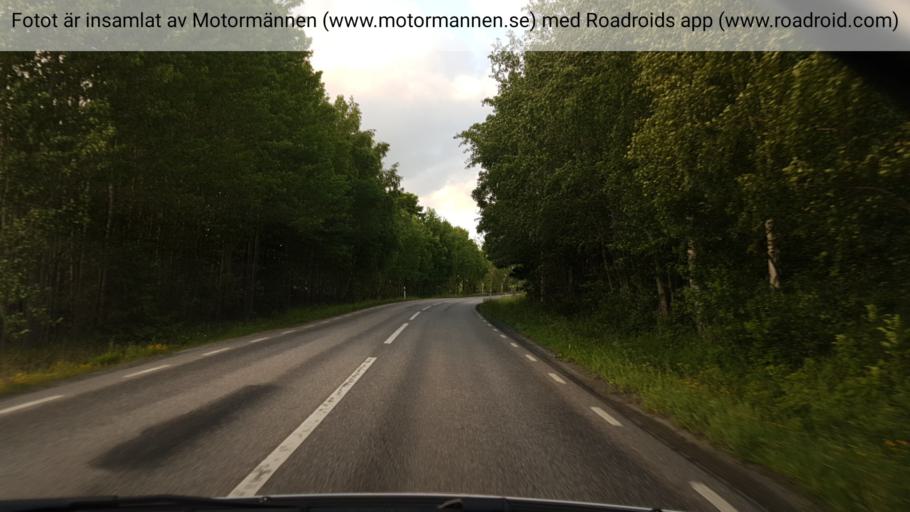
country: SE
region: OErebro
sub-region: Nora Kommun
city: As
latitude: 59.4830
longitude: 14.9243
